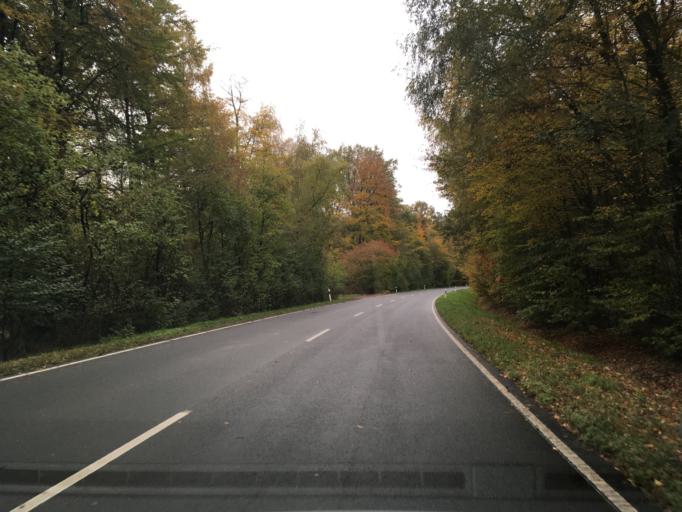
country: DE
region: North Rhine-Westphalia
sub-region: Regierungsbezirk Munster
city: Velen
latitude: 51.8770
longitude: 7.0028
